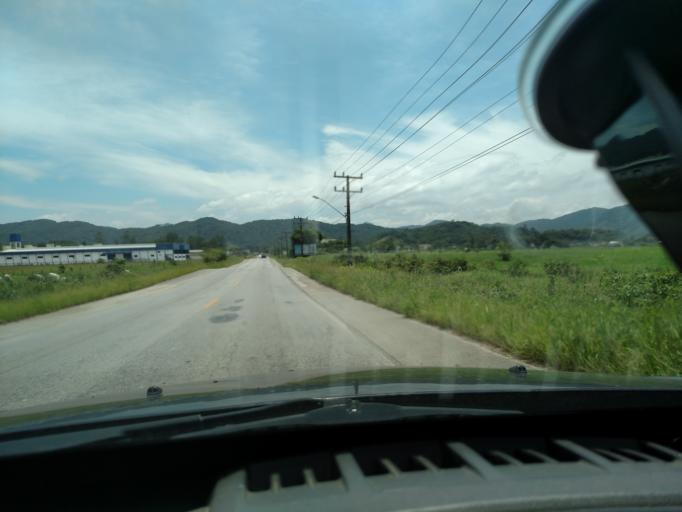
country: BR
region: Santa Catarina
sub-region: Gaspar
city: Gaspar
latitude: -26.9187
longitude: -48.9334
